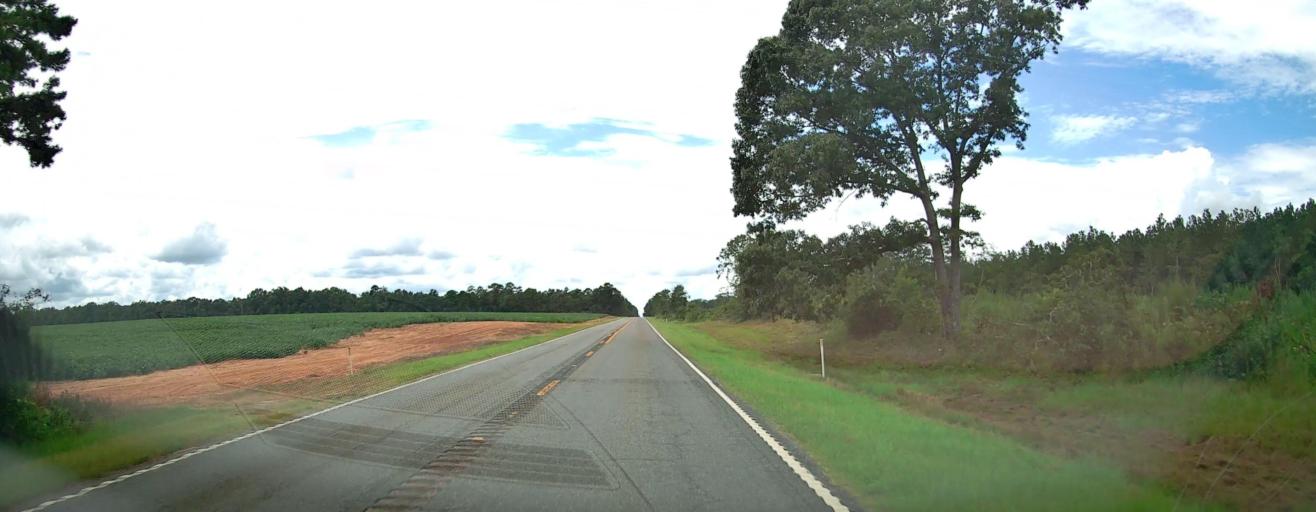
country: US
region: Georgia
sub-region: Dooly County
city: Unadilla
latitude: 32.2908
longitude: -83.8402
